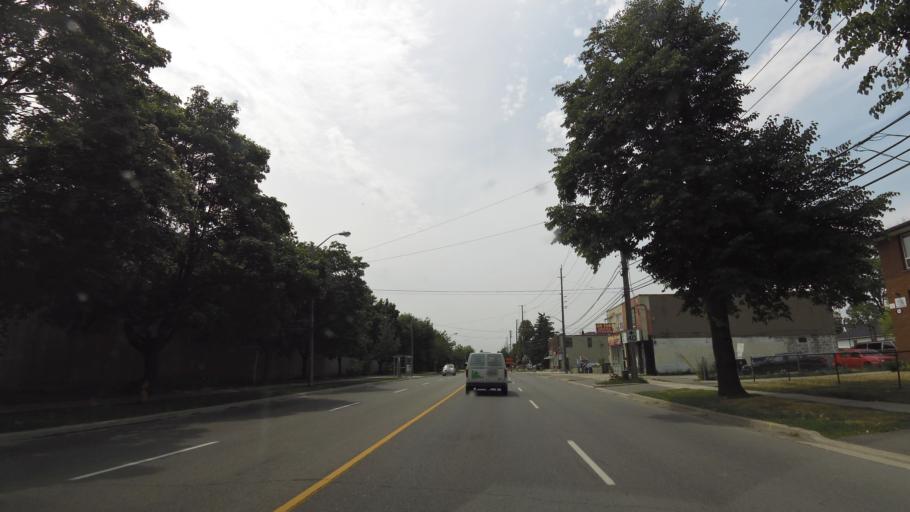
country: CA
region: Ontario
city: Etobicoke
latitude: 43.6040
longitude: -79.5352
